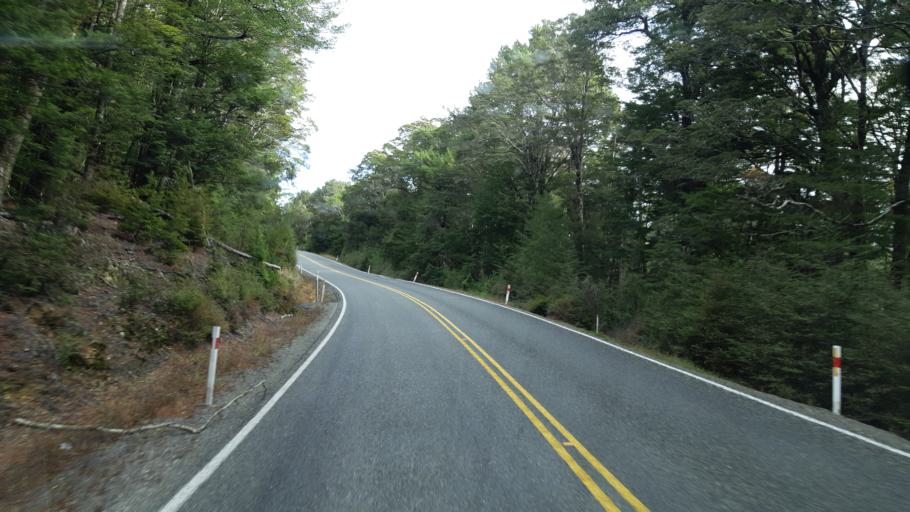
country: NZ
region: Tasman
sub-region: Tasman District
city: Wakefield
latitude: -41.7807
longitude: 172.9069
